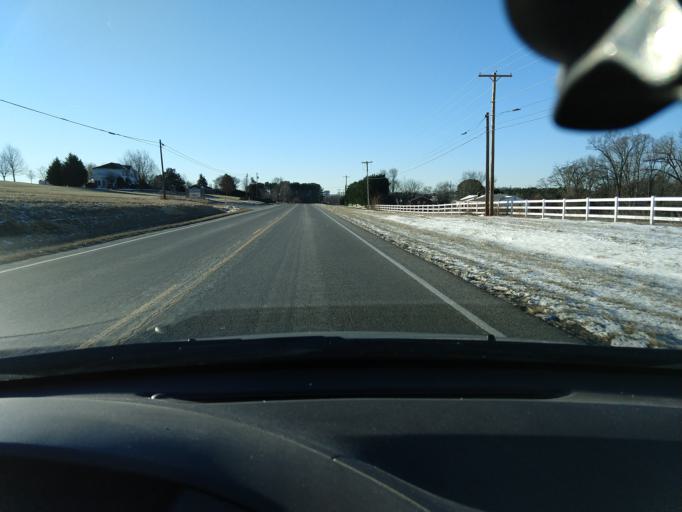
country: US
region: Virginia
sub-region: City of Bedford
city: Bedford
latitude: 37.3045
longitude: -79.5362
